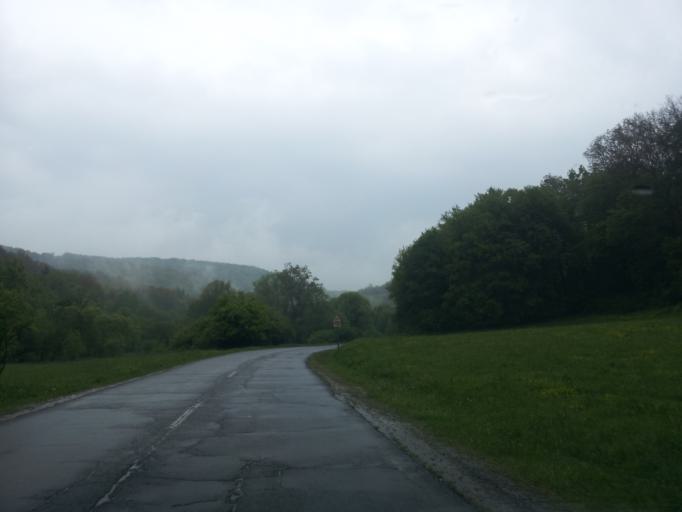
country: HU
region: Baranya
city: Komlo
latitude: 46.1985
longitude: 18.3041
